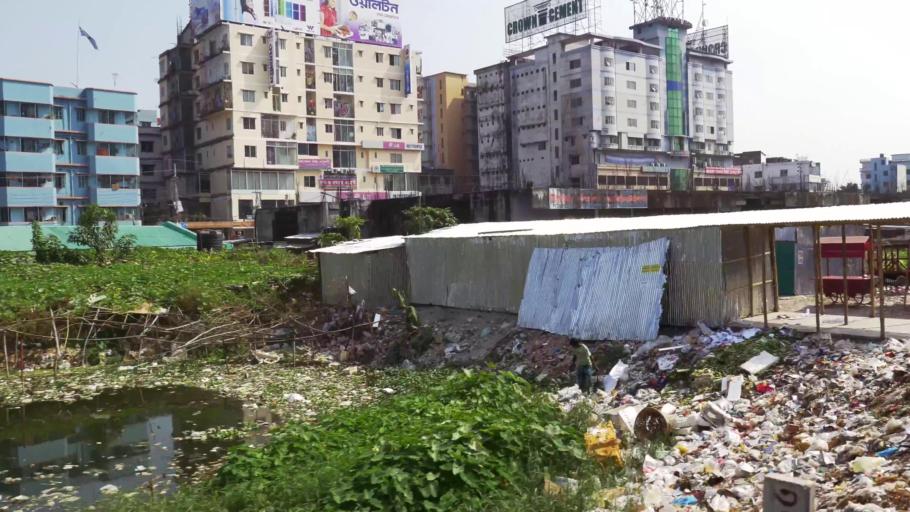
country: BD
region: Dhaka
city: Tungi
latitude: 23.8862
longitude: 90.4069
